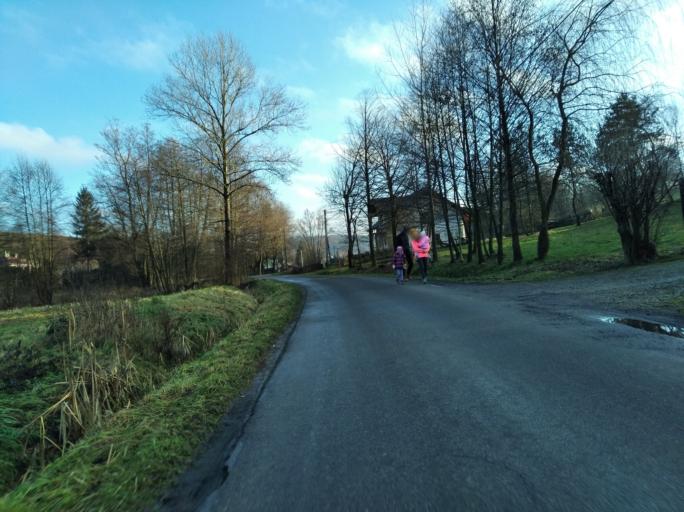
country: PL
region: Subcarpathian Voivodeship
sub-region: Powiat strzyzowski
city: Czudec
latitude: 49.9453
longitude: 21.8068
